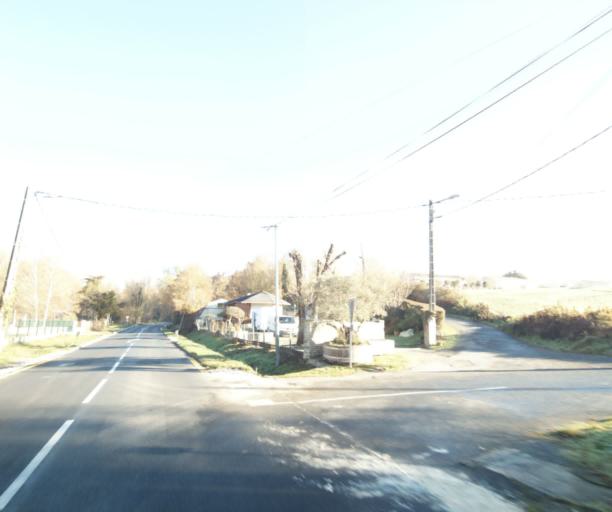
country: FR
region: Poitou-Charentes
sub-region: Departement de la Charente-Maritime
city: Fontcouverte
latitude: 45.7560
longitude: -0.5636
